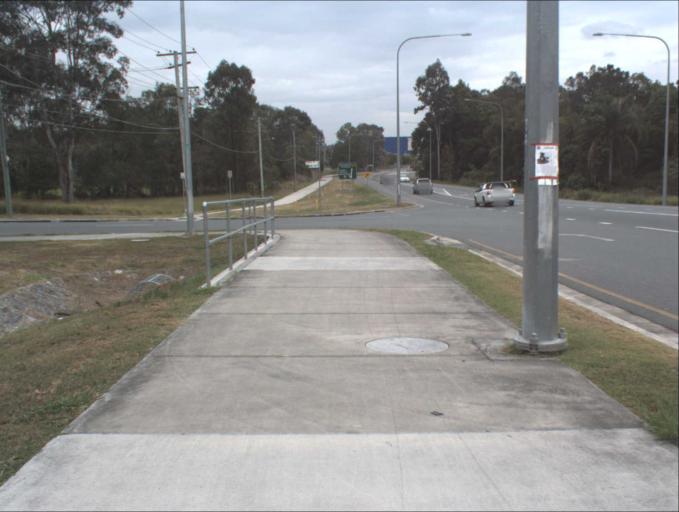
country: AU
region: Queensland
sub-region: Logan
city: Slacks Creek
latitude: -27.6413
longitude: 153.1403
